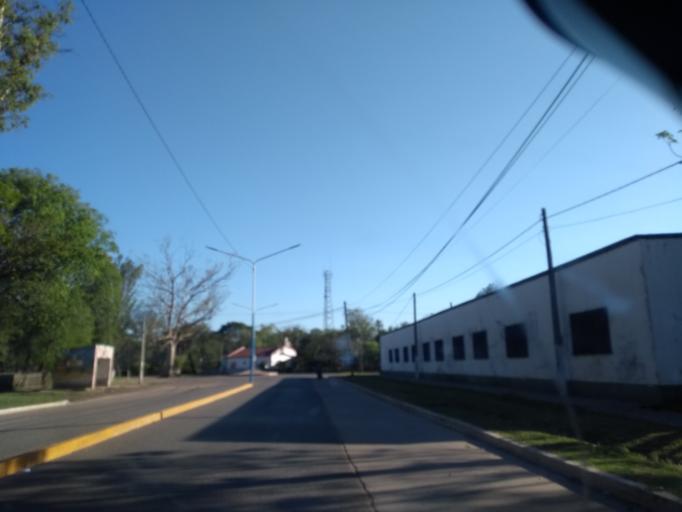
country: AR
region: Chaco
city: La Escondida
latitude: -27.1057
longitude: -59.4461
